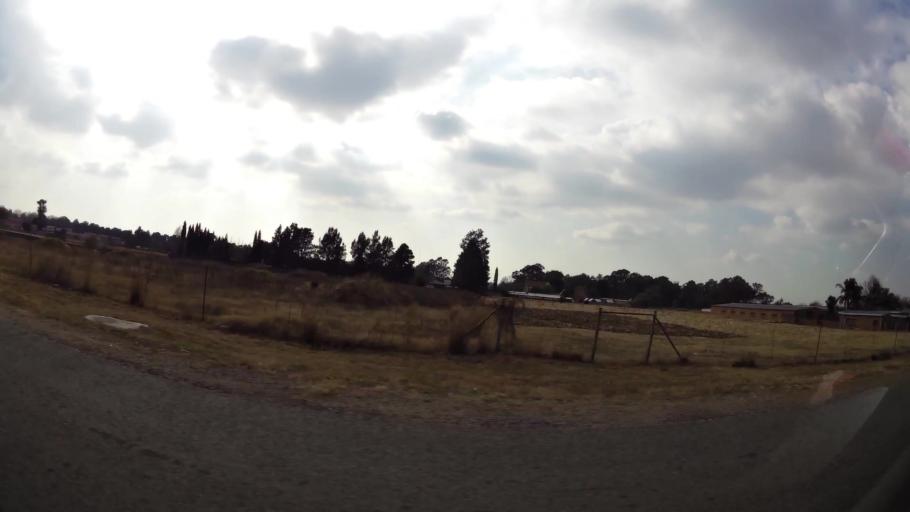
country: ZA
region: Gauteng
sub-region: Ekurhuleni Metropolitan Municipality
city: Benoni
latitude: -26.1283
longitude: 28.2643
